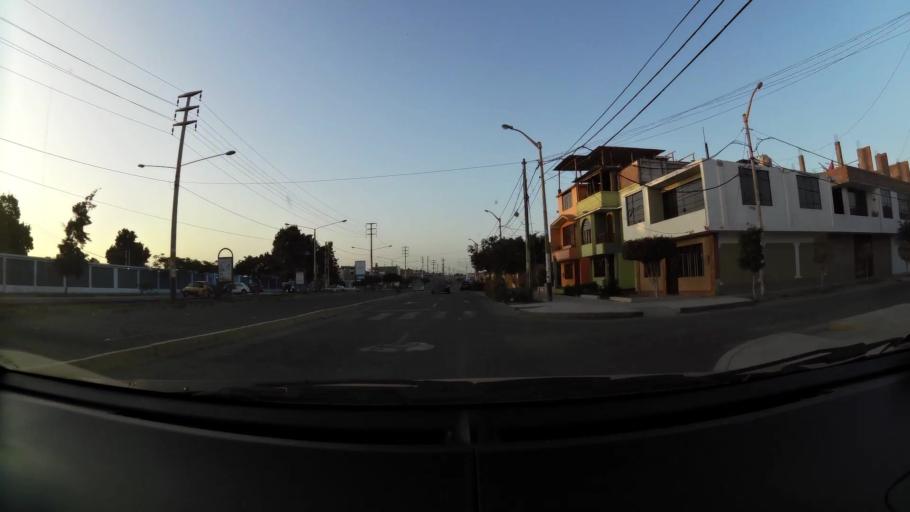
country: PE
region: Ancash
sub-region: Provincia de Santa
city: Buenos Aires
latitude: -9.1253
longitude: -78.5232
